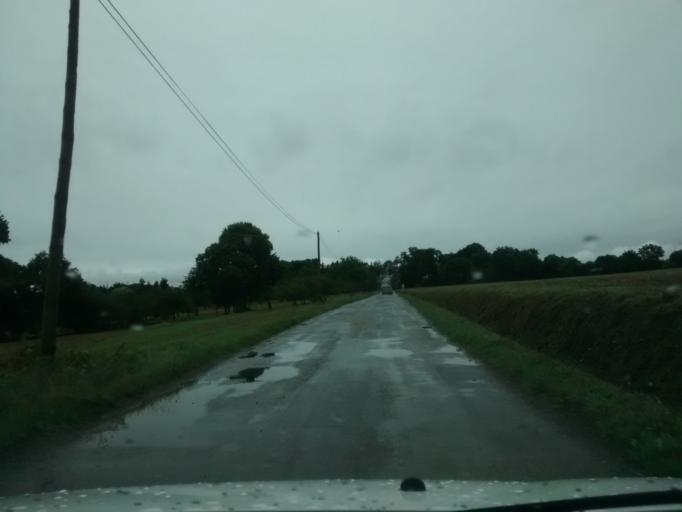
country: FR
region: Brittany
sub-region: Departement d'Ille-et-Vilaine
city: Vern-sur-Seiche
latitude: 48.0496
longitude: -1.5874
